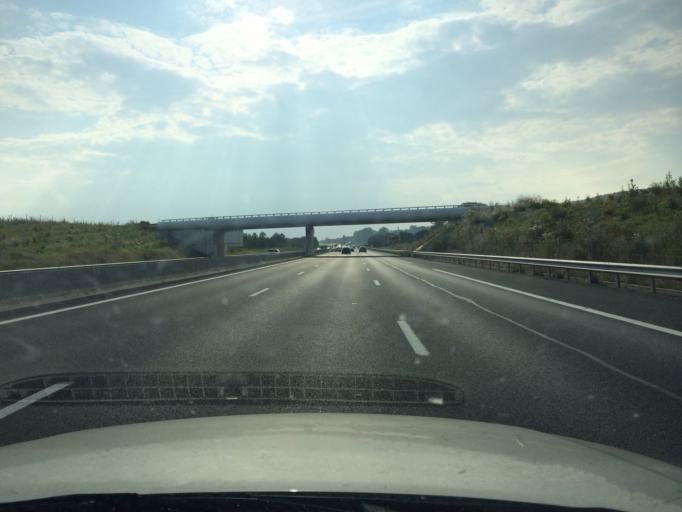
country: FR
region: Lower Normandy
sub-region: Departement du Calvados
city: Saint-Gatien-des-Bois
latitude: 49.2997
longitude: 0.2474
